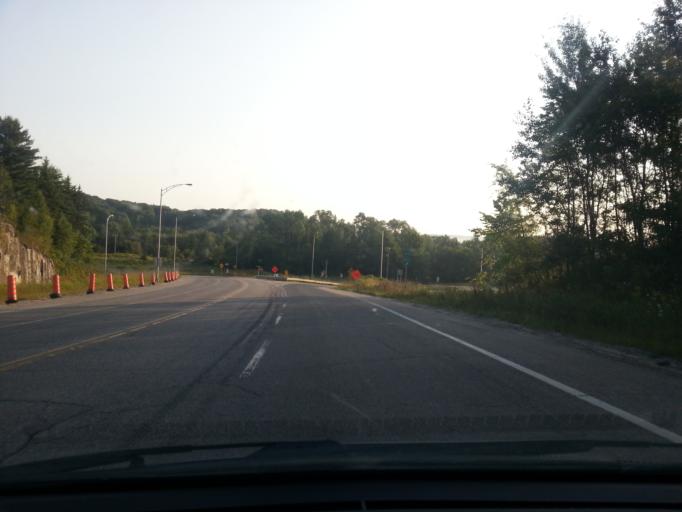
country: CA
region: Quebec
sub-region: Outaouais
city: Wakefield
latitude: 45.6524
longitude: -75.9374
